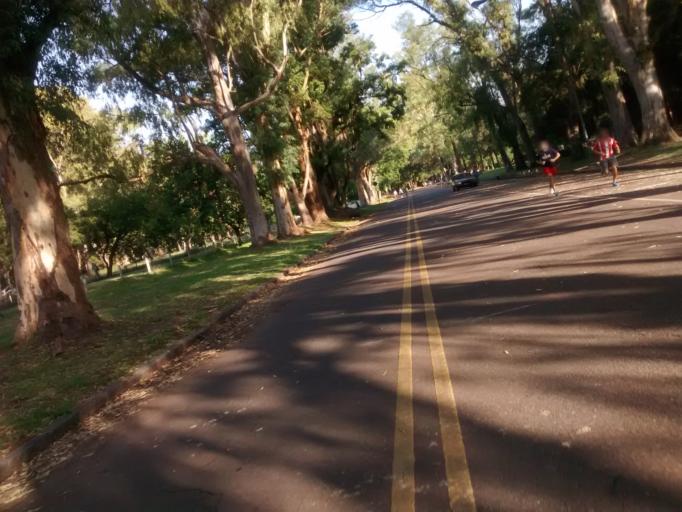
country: AR
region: Buenos Aires
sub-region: Partido de La Plata
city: La Plata
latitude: -34.9065
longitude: -57.9315
